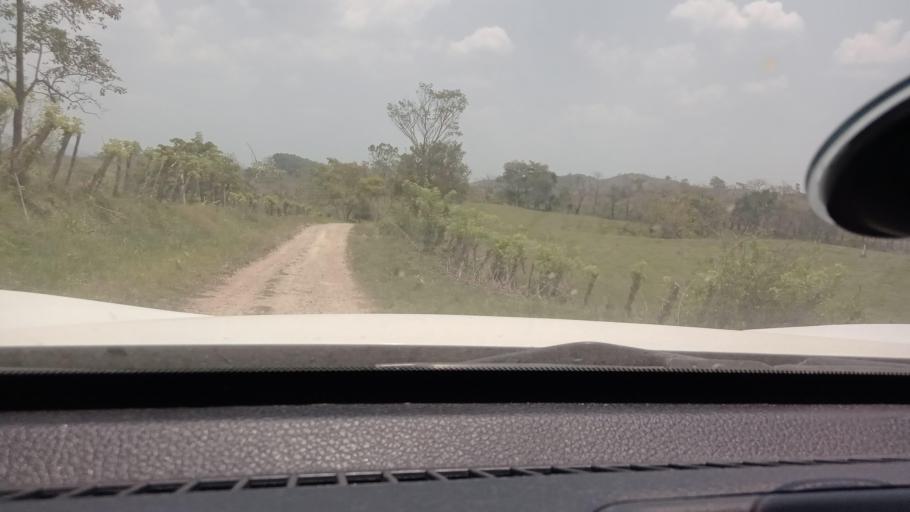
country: MX
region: Tabasco
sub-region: Huimanguillo
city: Francisco Rueda
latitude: 17.4850
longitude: -93.9365
